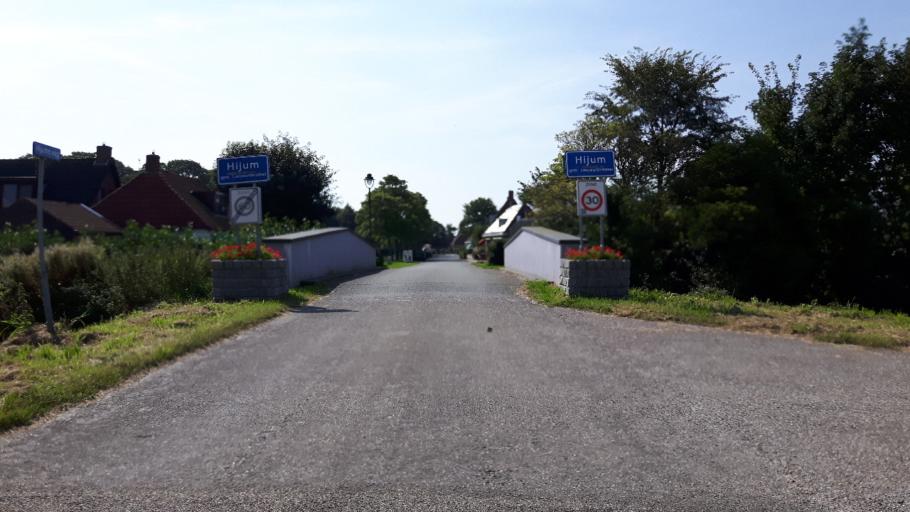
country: NL
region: Friesland
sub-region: Gemeente Ferwerderadiel
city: Hallum
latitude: 53.2935
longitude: 5.7677
